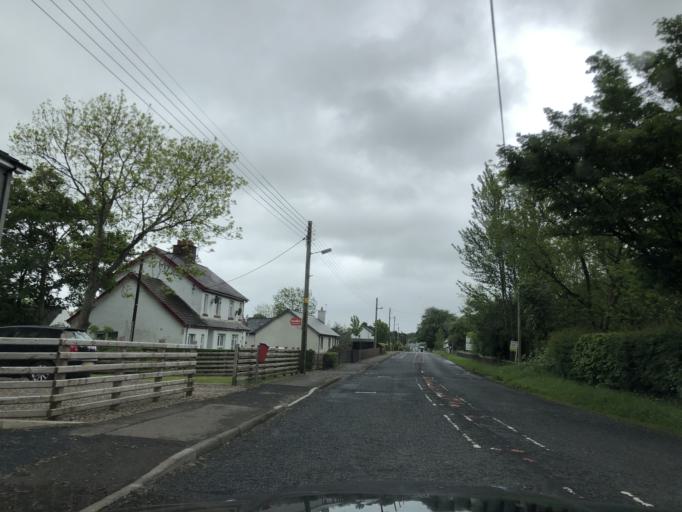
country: GB
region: Northern Ireland
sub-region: Ballymoney District
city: Ballymoney
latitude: 55.1230
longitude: -6.4783
